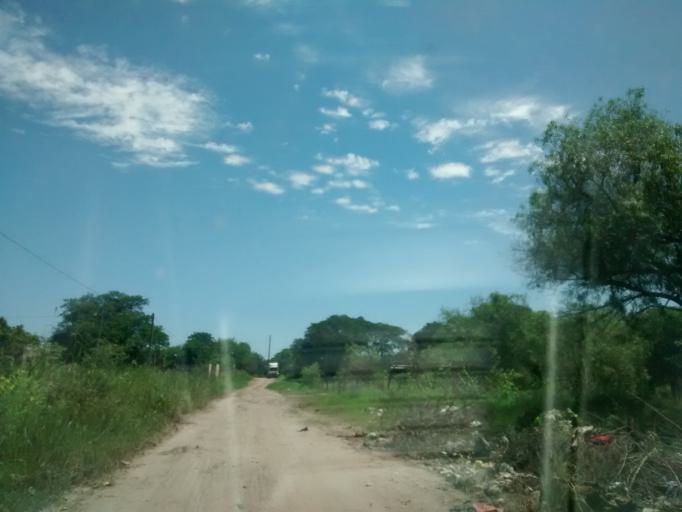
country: AR
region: Chaco
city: Resistencia
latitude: -27.4234
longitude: -58.9705
